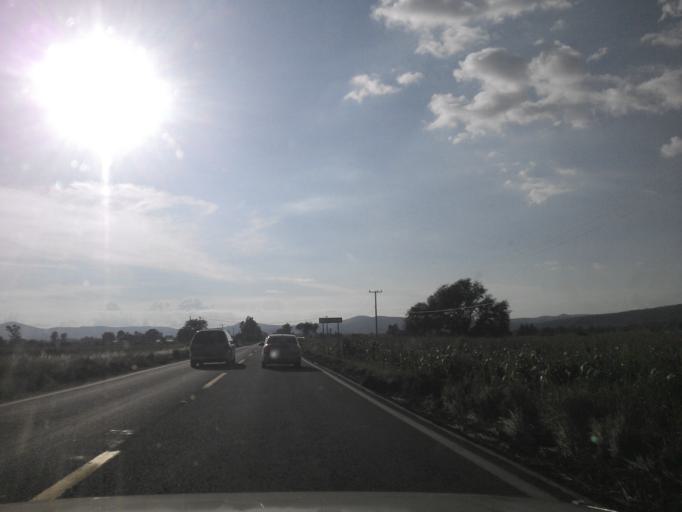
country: MX
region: Jalisco
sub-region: Tototlan
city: Nuevo Refugio de Afuera (Nuevo Refugio)
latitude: 20.5544
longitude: -102.6970
